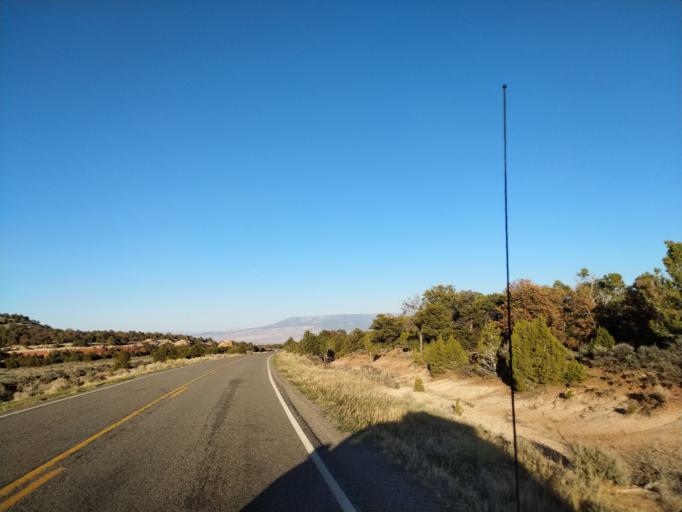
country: US
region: Colorado
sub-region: Mesa County
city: Redlands
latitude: 39.0089
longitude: -108.6820
